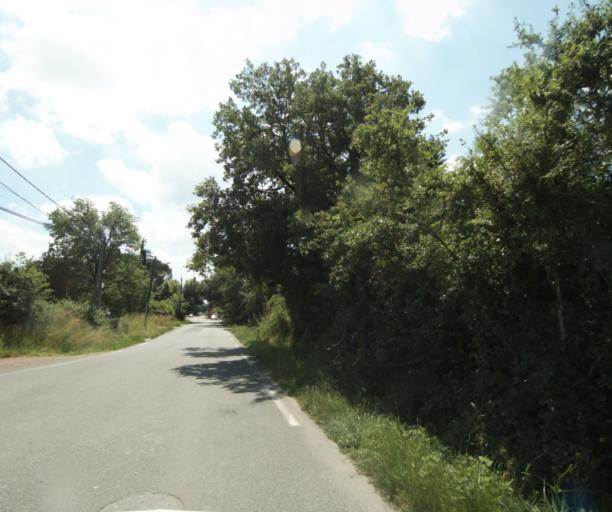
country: FR
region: Midi-Pyrenees
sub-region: Departement du Tarn-et-Garonne
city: Montauban
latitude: 44.0377
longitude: 1.3504
